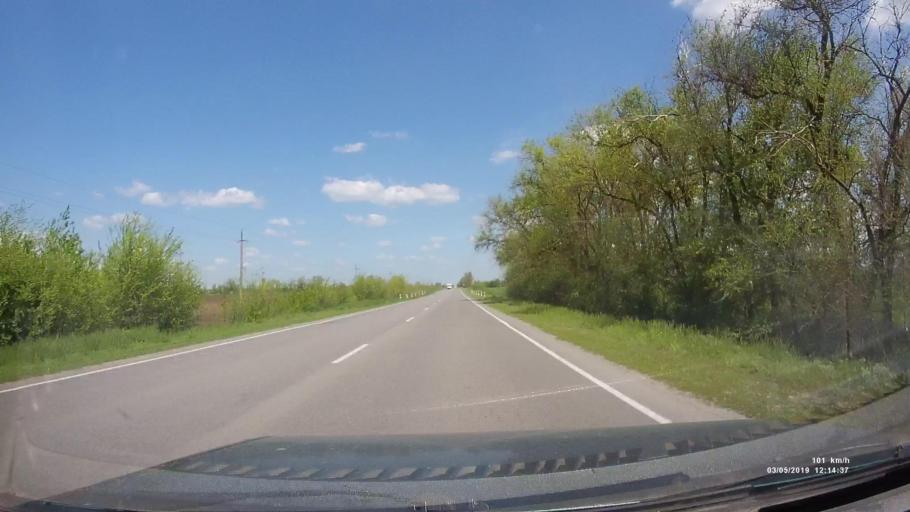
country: RU
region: Rostov
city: Melikhovskaya
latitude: 47.3466
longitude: 40.5653
